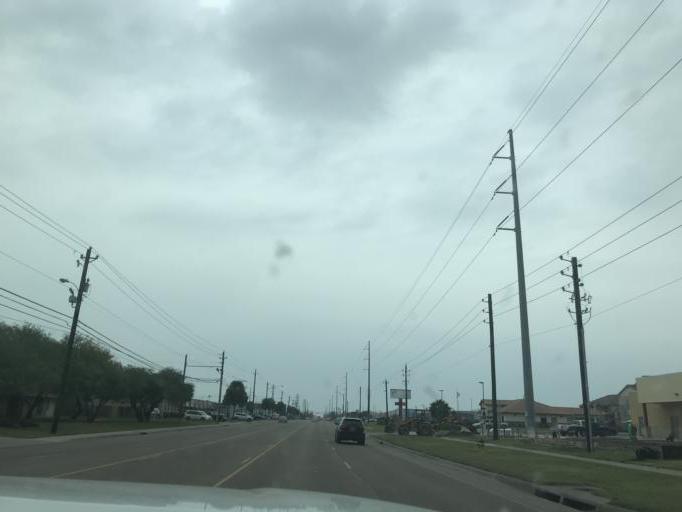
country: US
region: Texas
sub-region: Nueces County
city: Corpus Christi
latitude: 27.6943
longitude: -97.3679
